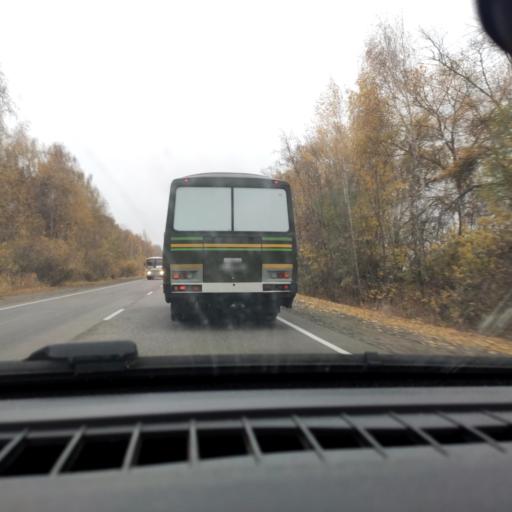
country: RU
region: Voronezj
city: Kolodeznyy
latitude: 51.3576
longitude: 39.0236
